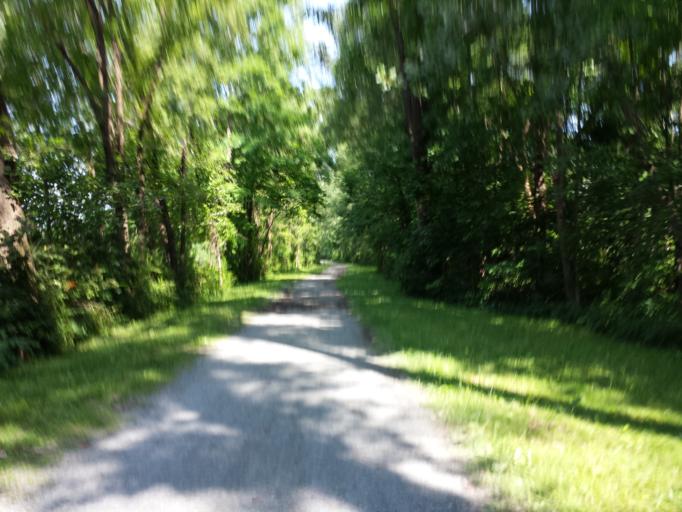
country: US
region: New York
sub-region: Saratoga County
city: Country Knolls
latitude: 42.9174
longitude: -73.7671
